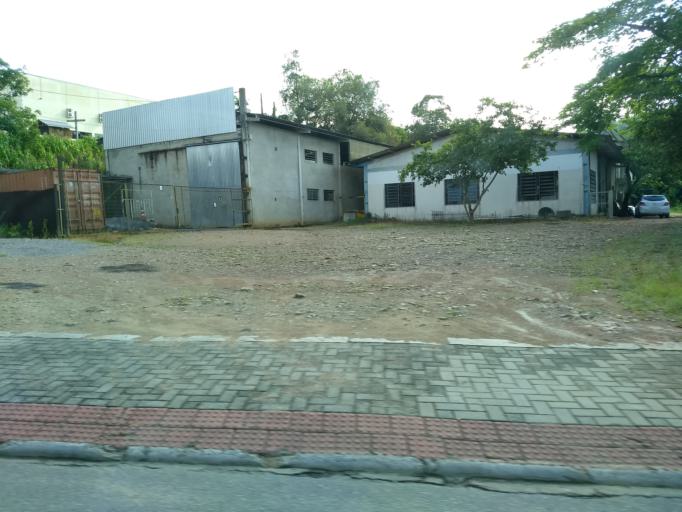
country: BR
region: Santa Catarina
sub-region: Jaragua Do Sul
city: Jaragua do Sul
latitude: -26.4552
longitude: -49.1072
